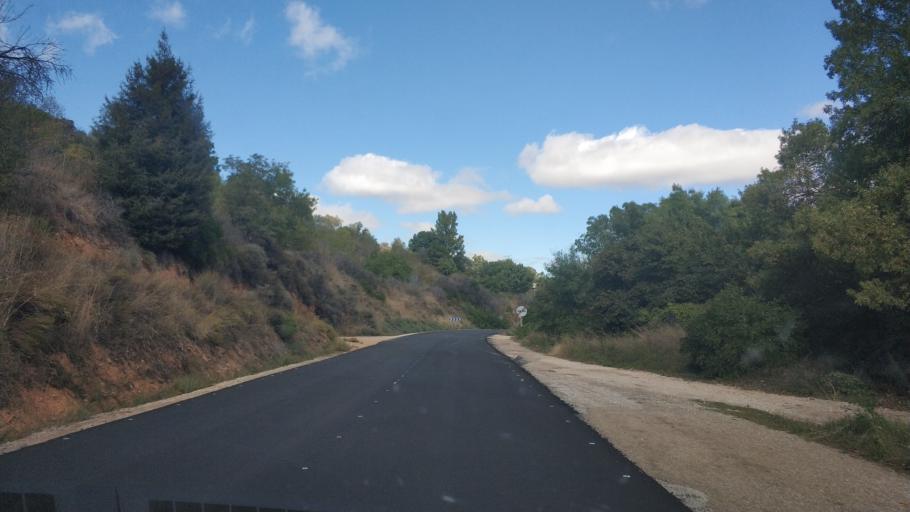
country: ES
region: Castille and Leon
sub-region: Provincia de Burgos
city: Covarrubias
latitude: 42.0557
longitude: -3.5242
